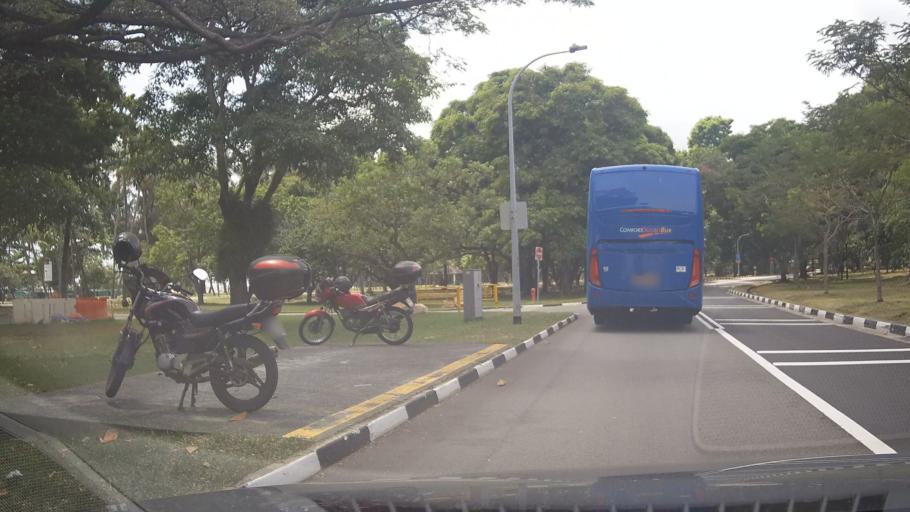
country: SG
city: Singapore
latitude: 1.2963
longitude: 103.8982
